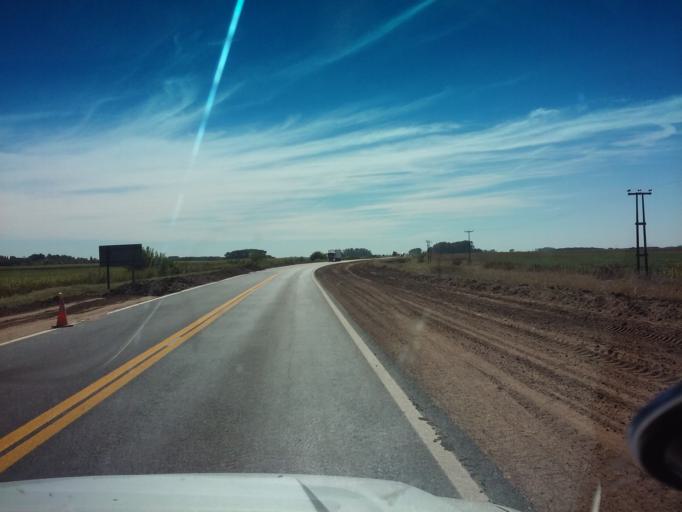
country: AR
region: Buenos Aires
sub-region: Partido de Nueve de Julio
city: Nueve de Julio
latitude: -35.3549
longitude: -60.6966
